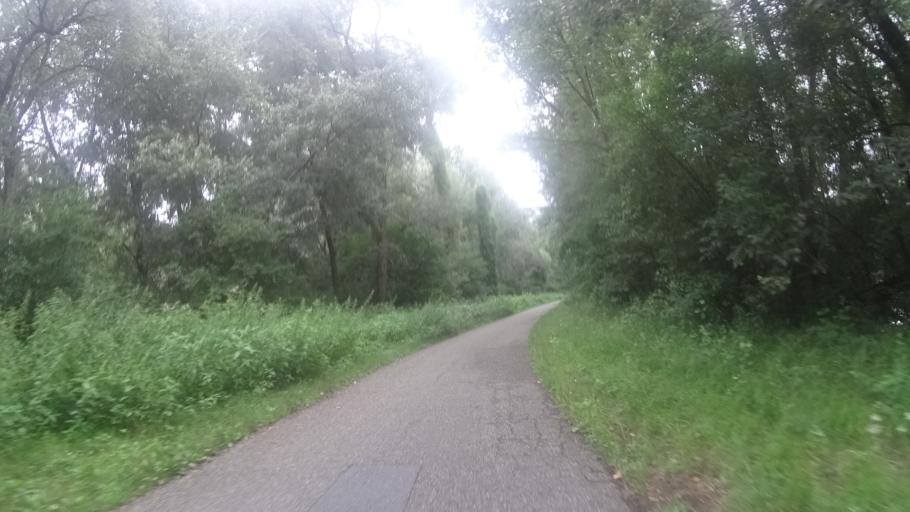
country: FR
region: Alsace
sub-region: Departement du Bas-Rhin
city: Seltz
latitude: 48.9064
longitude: 8.1299
